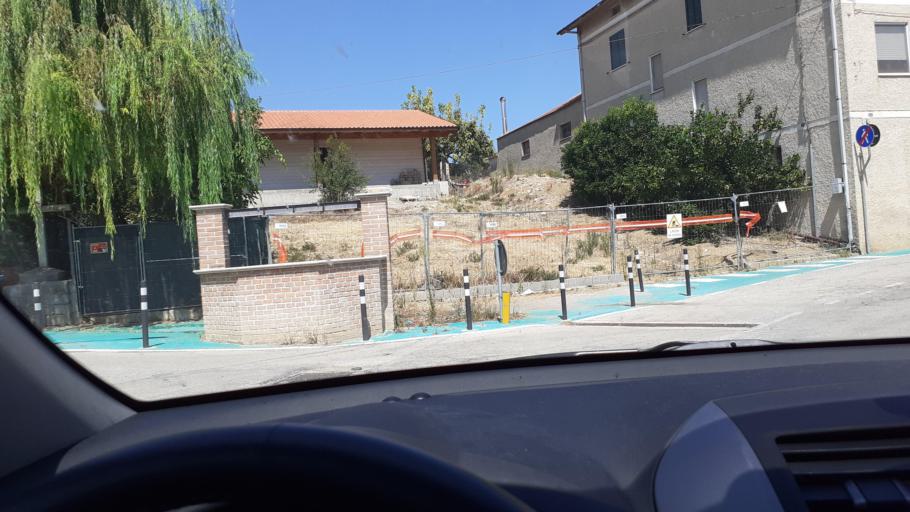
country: IT
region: Abruzzo
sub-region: Provincia di Chieti
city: Santa Maria Imbaro
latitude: 42.2209
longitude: 14.4509
